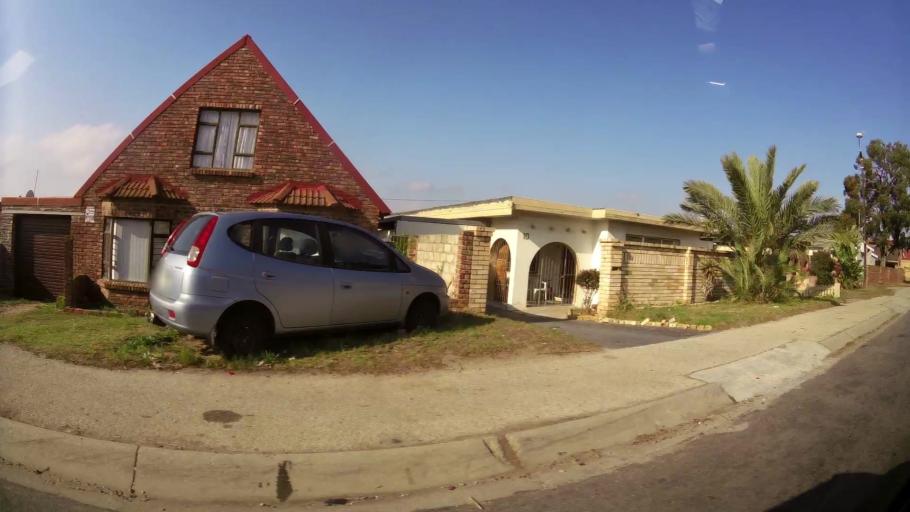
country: ZA
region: Eastern Cape
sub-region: Nelson Mandela Bay Metropolitan Municipality
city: Port Elizabeth
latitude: -33.9218
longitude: 25.5311
